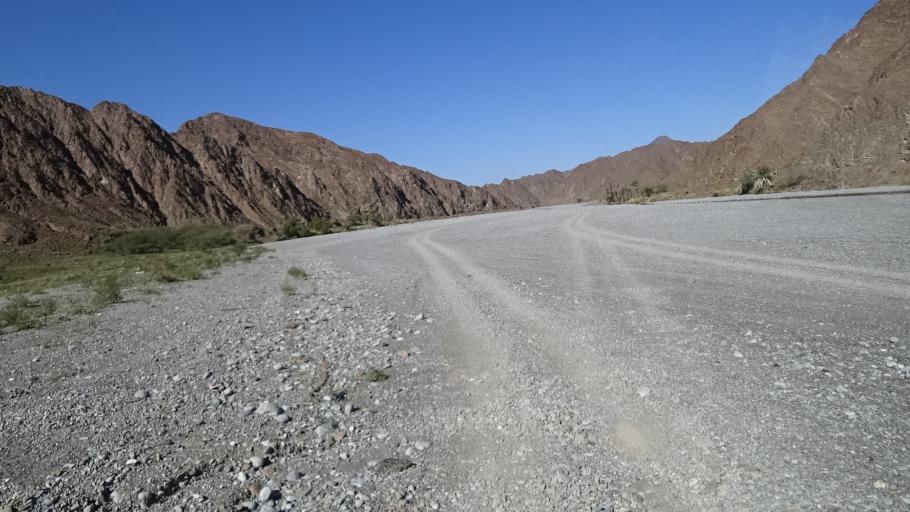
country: OM
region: Al Batinah
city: Bayt al `Awabi
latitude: 23.4042
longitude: 57.6659
